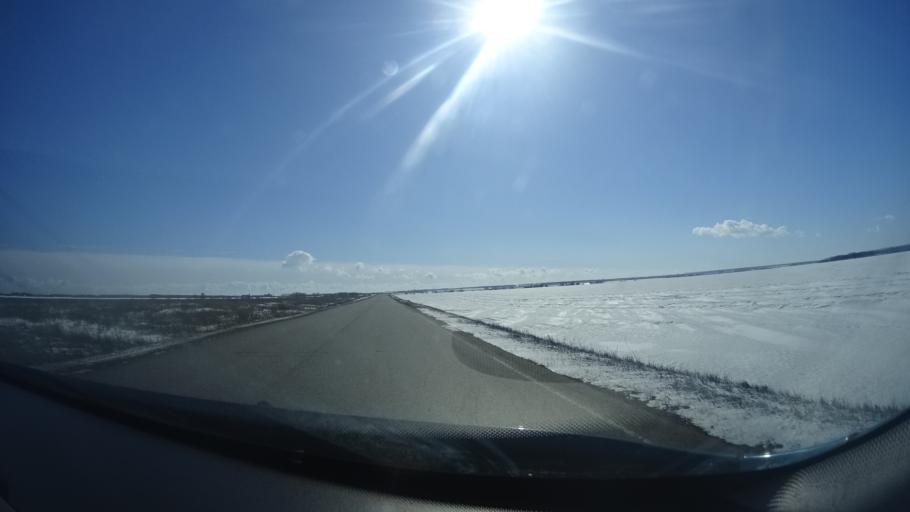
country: RU
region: Bashkortostan
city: Avdon
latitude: 54.5957
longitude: 55.8525
